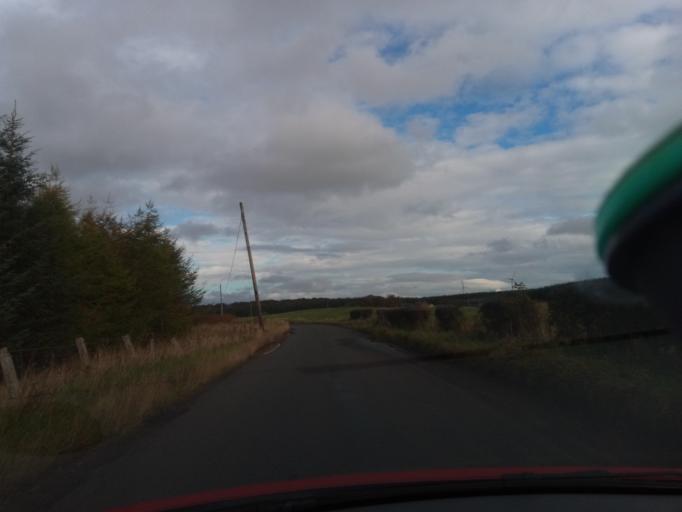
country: GB
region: Scotland
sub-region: South Lanarkshire
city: Carnwath
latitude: 55.7493
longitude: -3.6051
